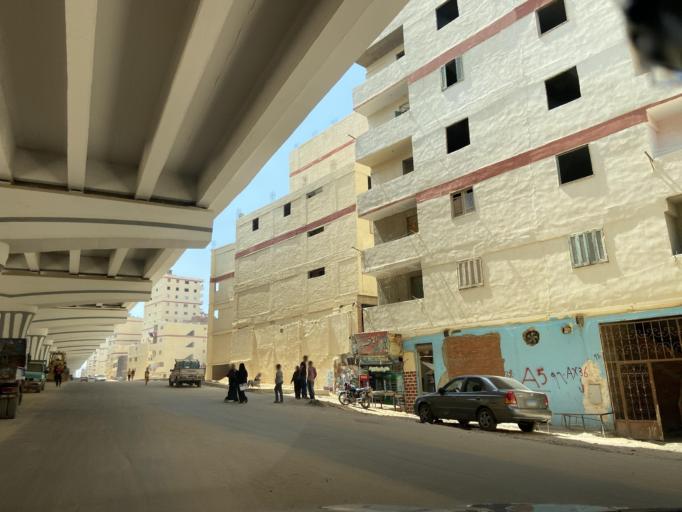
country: EG
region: Muhafazat al Qahirah
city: Cairo
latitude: 30.0680
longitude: 31.3850
